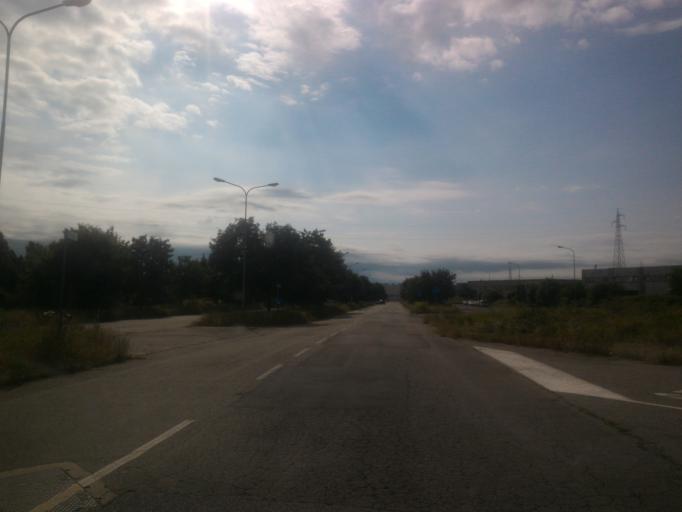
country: IT
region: Piedmont
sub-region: Provincia di Torino
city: Frossasco
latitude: 44.9019
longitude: 7.3613
